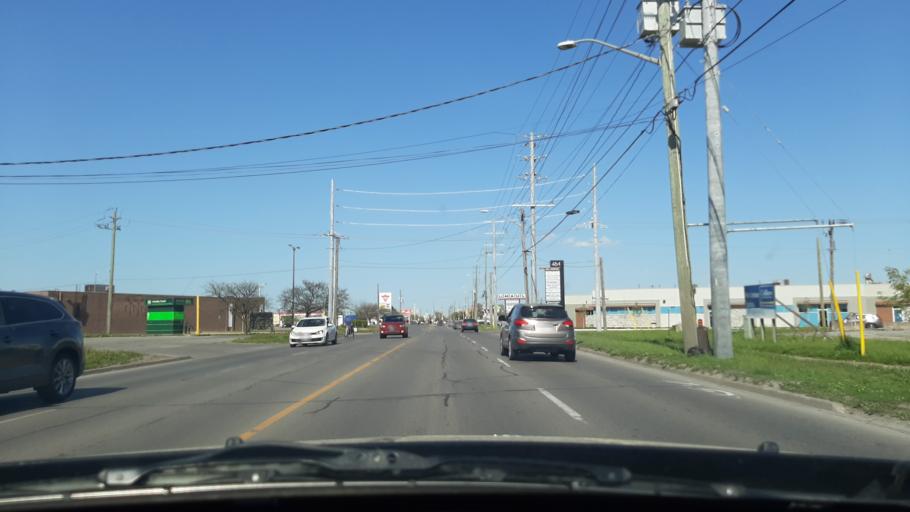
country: CA
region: Ontario
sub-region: Regional Municipality of Niagara
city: St. Catharines
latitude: 43.1735
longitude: -79.2184
